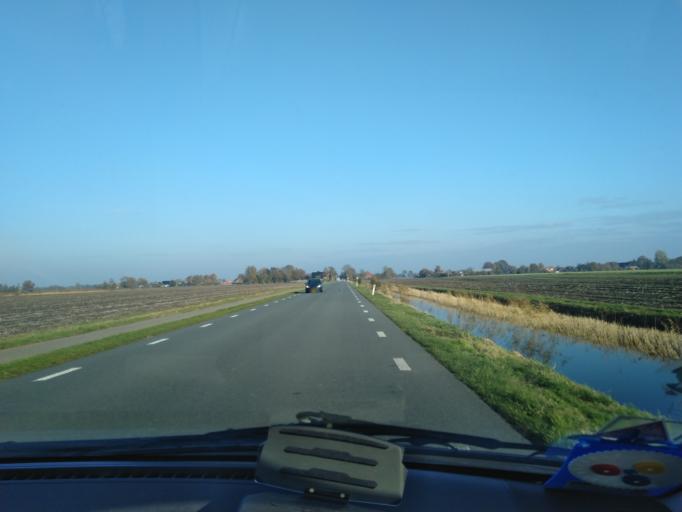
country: NL
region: Groningen
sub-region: Gemeente Hoogezand-Sappemeer
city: Hoogezand
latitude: 53.1206
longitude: 6.7618
